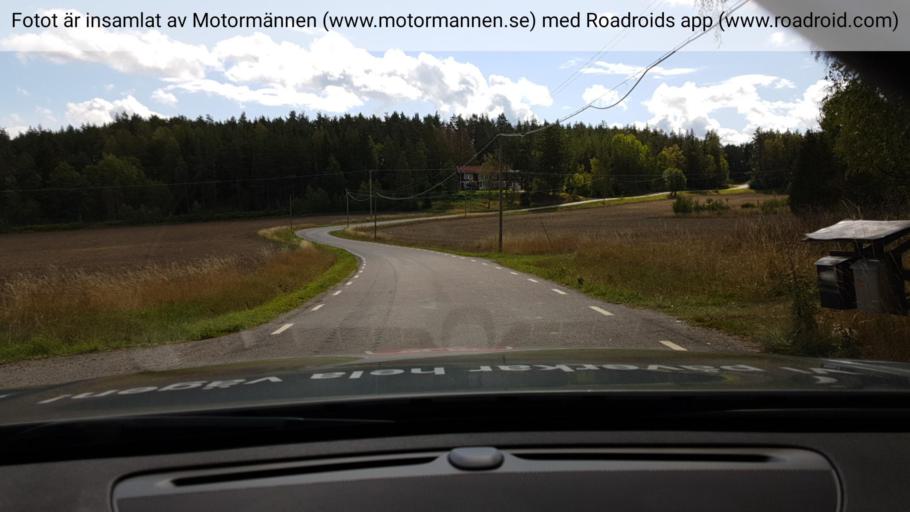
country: SE
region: Soedermanland
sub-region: Strangnas Kommun
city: Stallarholmen
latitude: 59.3955
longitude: 17.2669
